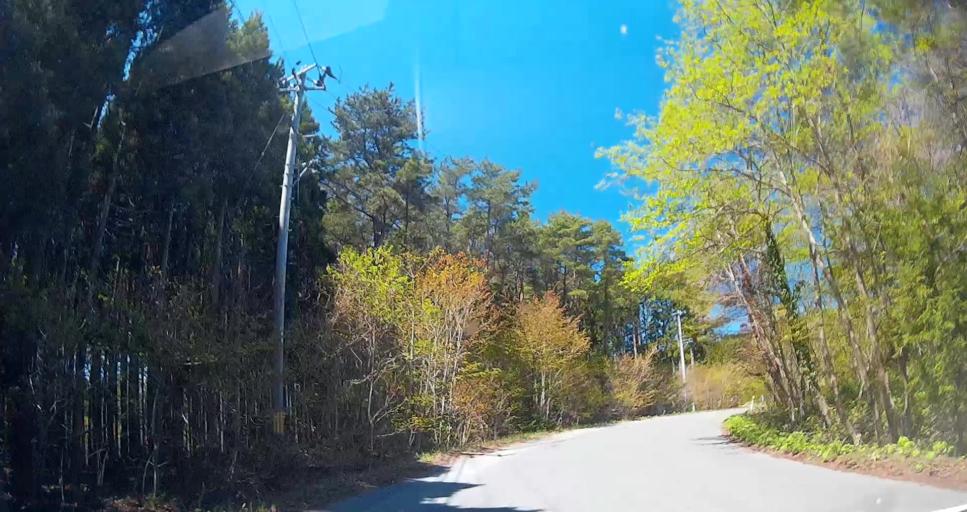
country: JP
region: Aomori
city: Mutsu
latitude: 41.2499
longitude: 141.3903
